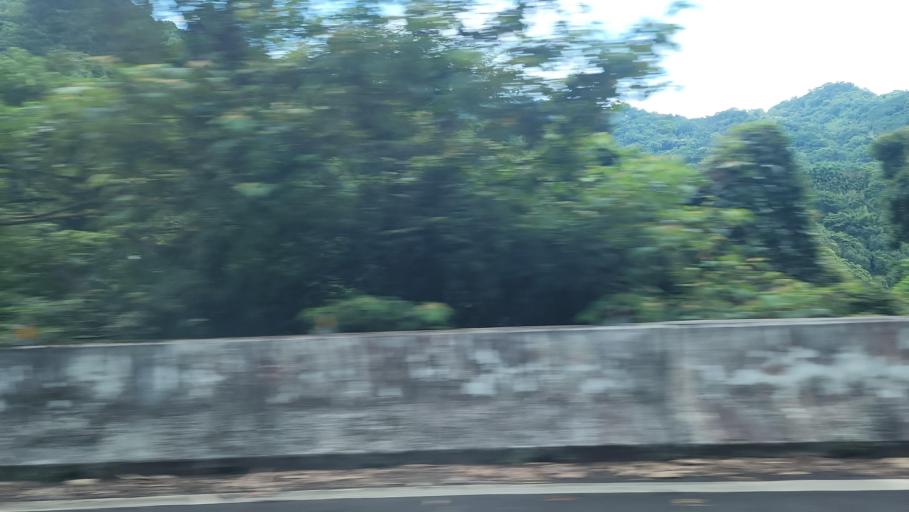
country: TW
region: Taipei
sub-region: Taipei
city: Banqiao
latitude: 24.8930
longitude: 121.4250
